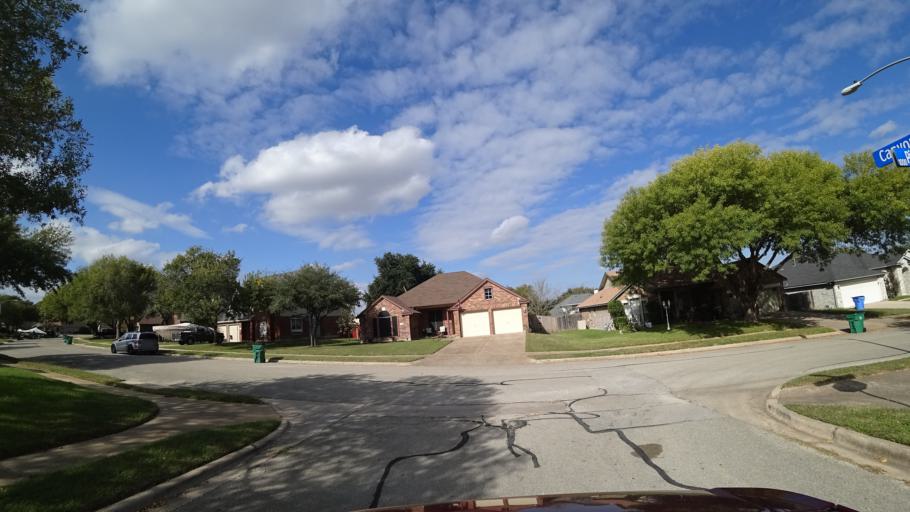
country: US
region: Texas
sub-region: Travis County
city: Pflugerville
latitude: 30.4361
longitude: -97.6323
